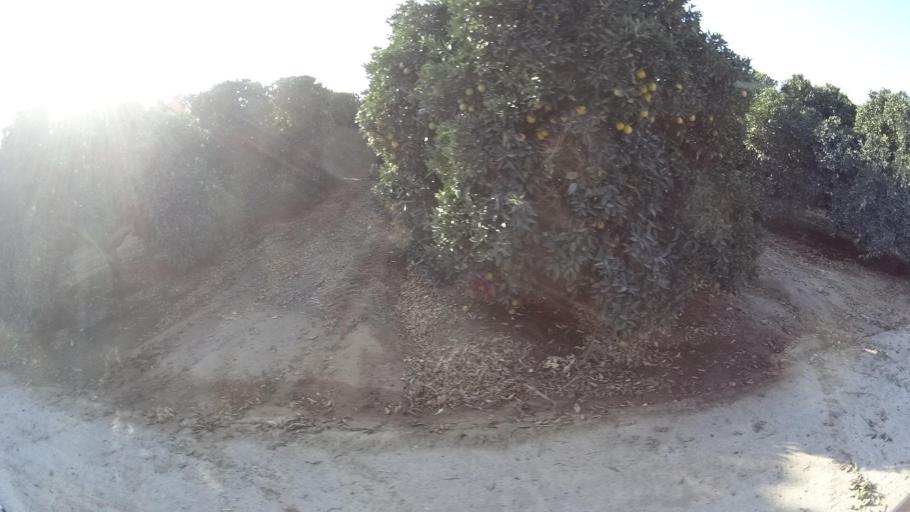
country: US
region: California
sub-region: Tulare County
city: Richgrove
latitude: 35.7763
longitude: -119.0853
